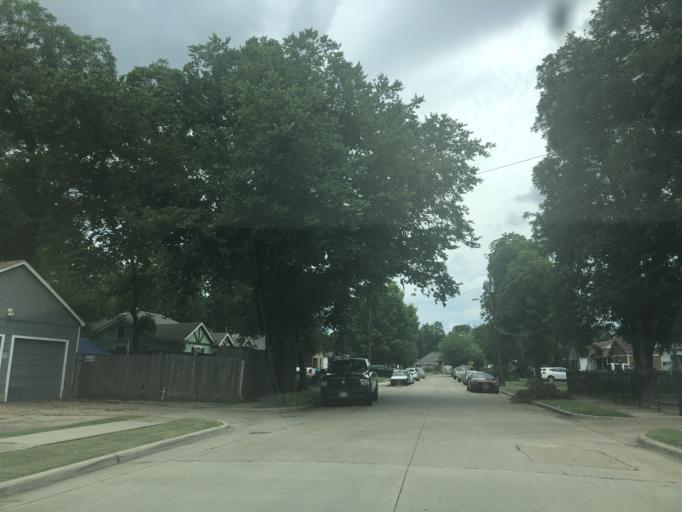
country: US
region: Texas
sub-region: Dallas County
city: Irving
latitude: 32.8011
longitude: -96.9333
